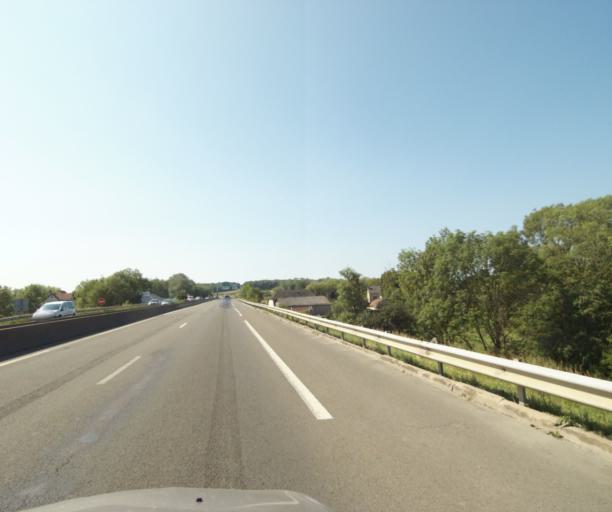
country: FR
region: Champagne-Ardenne
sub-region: Departement des Ardennes
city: Prix-les-Mezieres
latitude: 49.7565
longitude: 4.7027
